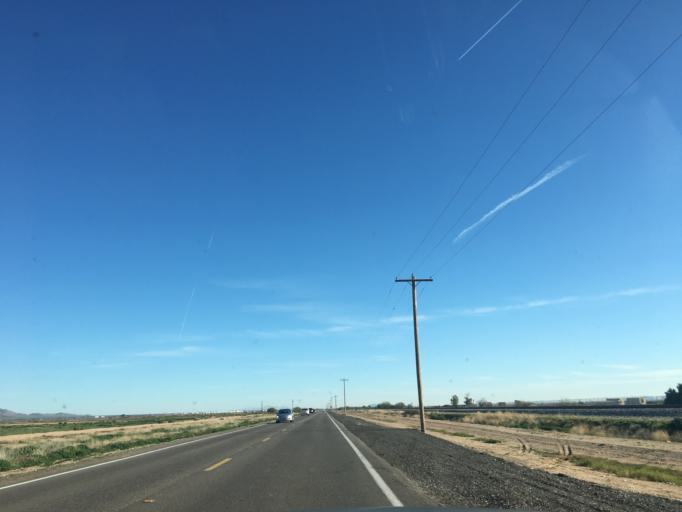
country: US
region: Arizona
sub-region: Pinal County
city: Maricopa
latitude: 33.0126
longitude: -111.9765
